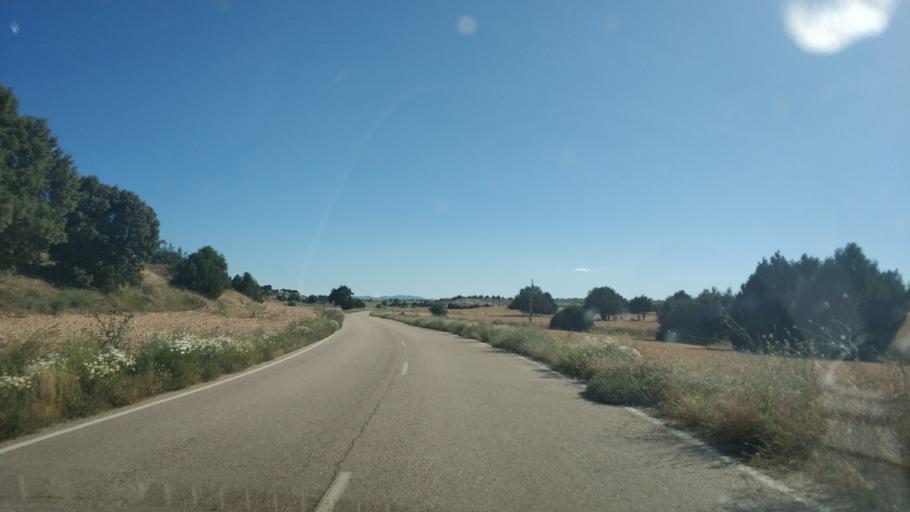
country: ES
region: Castille and Leon
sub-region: Provincia de Soria
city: San Esteban de Gormaz
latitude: 41.4867
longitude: -3.2089
